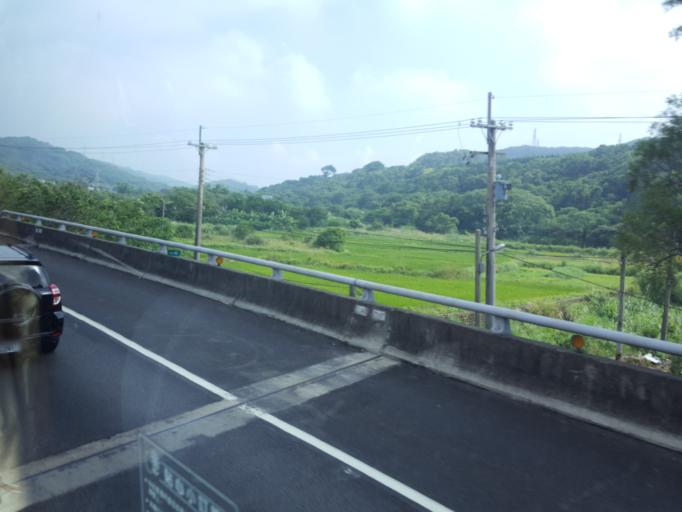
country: TW
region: Taiwan
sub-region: Hsinchu
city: Zhubei
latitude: 24.8850
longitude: 121.0877
